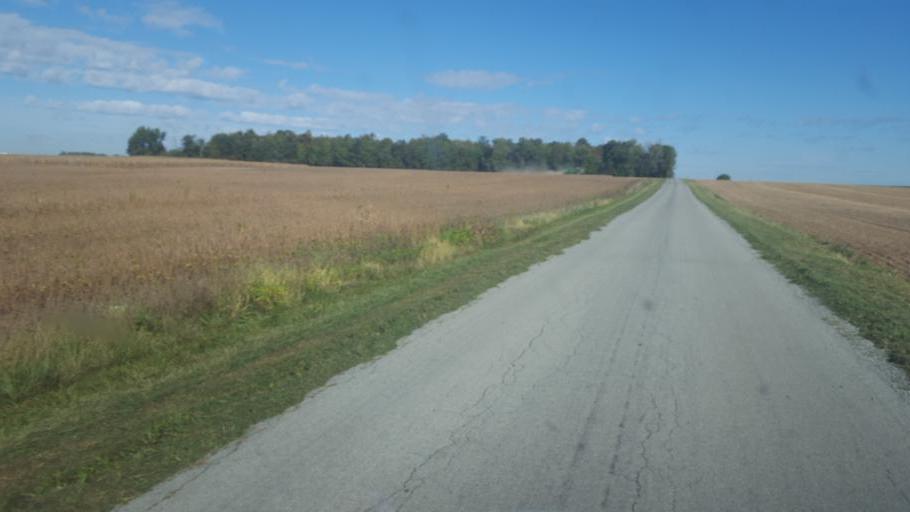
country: US
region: Ohio
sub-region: Wyandot County
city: Upper Sandusky
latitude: 40.7925
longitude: -83.2173
